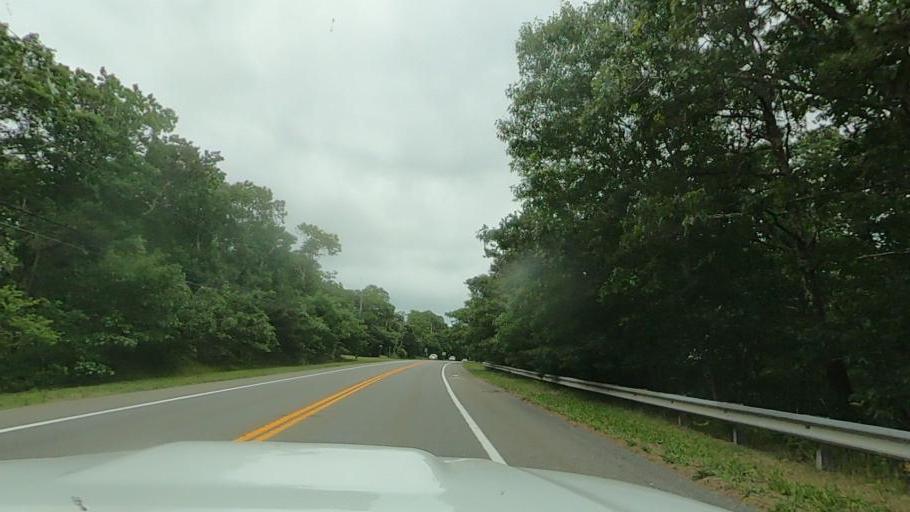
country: US
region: Massachusetts
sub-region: Barnstable County
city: Wellfleet
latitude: 41.9659
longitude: -70.0278
